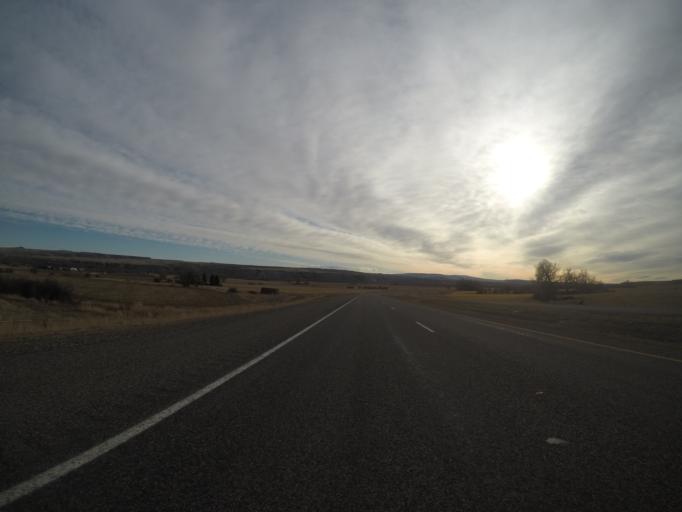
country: US
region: Montana
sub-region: Yellowstone County
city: Laurel
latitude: 45.5420
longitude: -108.8561
